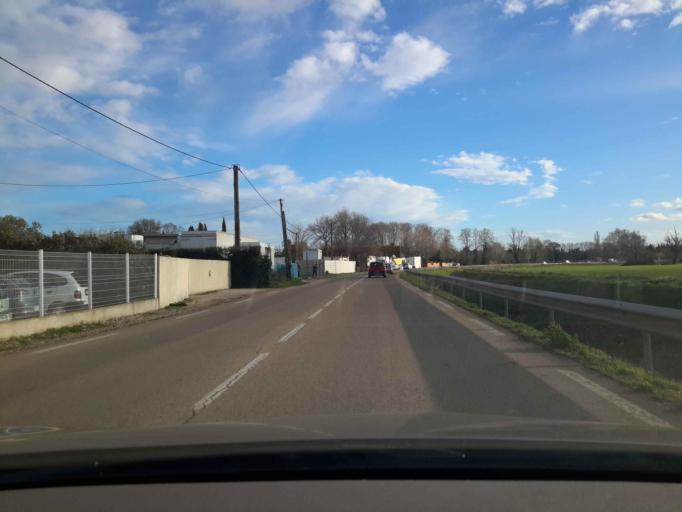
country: FR
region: Languedoc-Roussillon
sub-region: Departement du Gard
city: Caissargues
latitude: 43.7958
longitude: 4.3523
